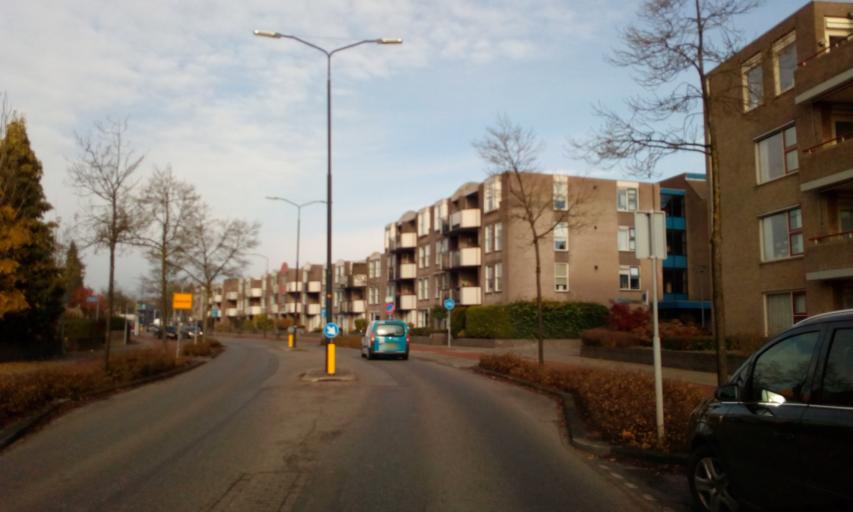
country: NL
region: Gelderland
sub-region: Gemeente Apeldoorn
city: Apeldoorn
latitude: 52.2106
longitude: 5.9569
